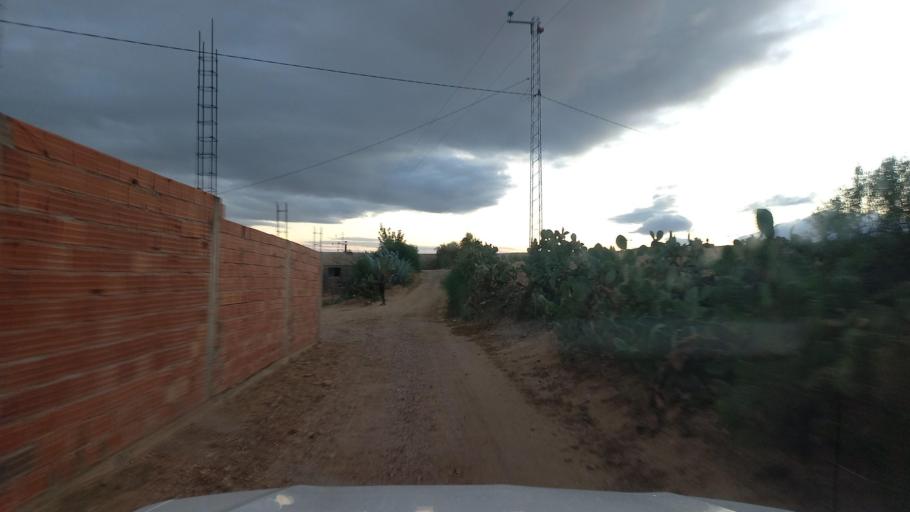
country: TN
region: Al Qasrayn
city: Kasserine
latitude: 35.2553
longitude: 8.9334
